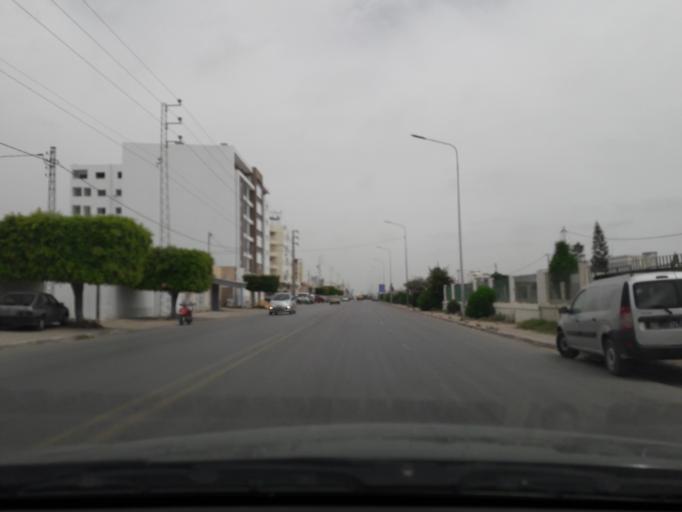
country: TN
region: Safaqis
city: Al Qarmadah
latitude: 34.7968
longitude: 10.7607
